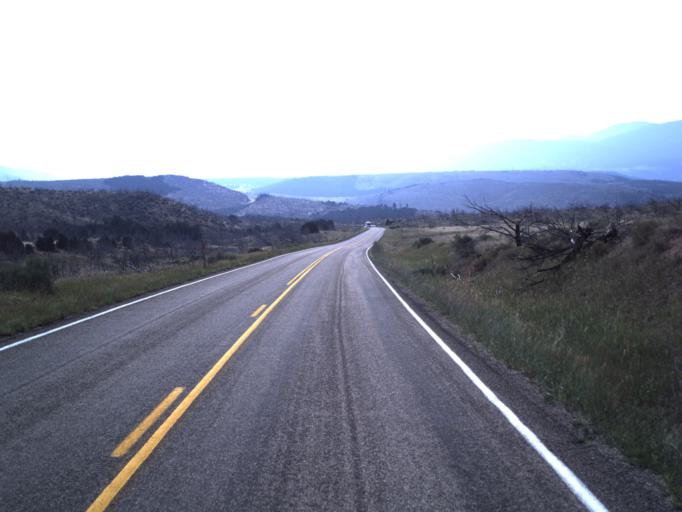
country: US
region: Utah
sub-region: Daggett County
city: Manila
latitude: 40.9496
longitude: -109.4444
